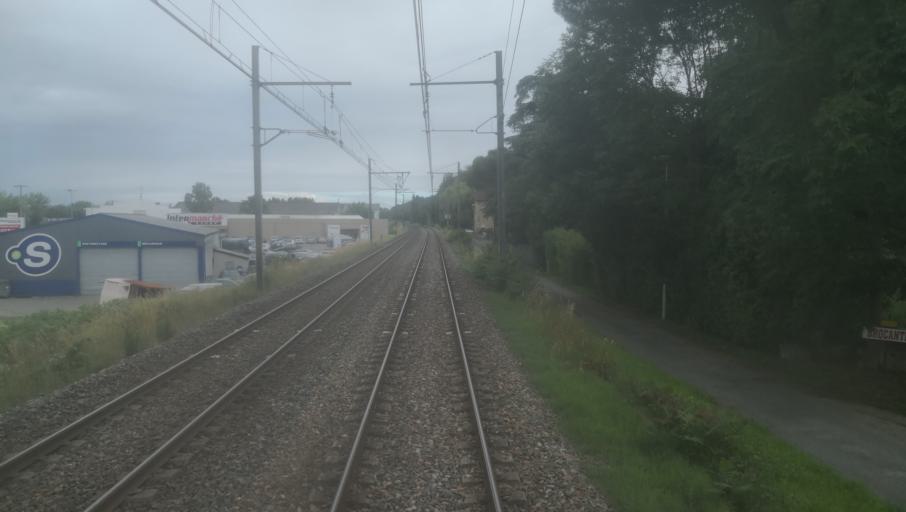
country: FR
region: Aquitaine
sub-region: Departement du Lot-et-Garonne
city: Port-Sainte-Marie
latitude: 44.2542
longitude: 0.3763
